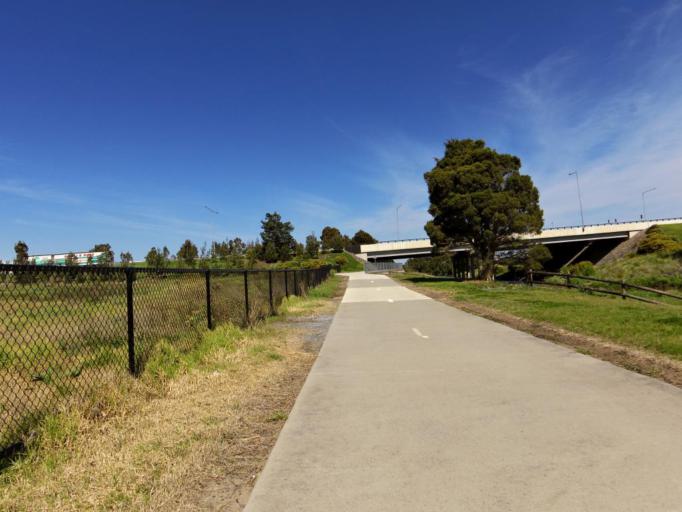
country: AU
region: Victoria
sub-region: Greater Dandenong
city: Keysborough
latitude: -38.0106
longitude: 145.1911
